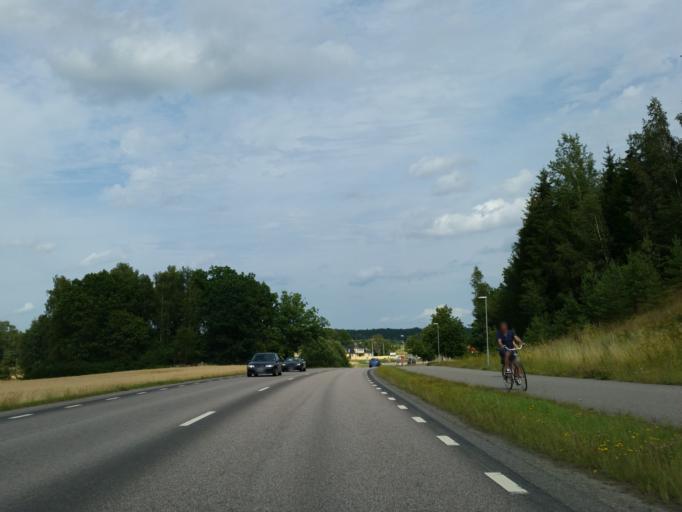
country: SE
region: Soedermanland
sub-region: Strangnas Kommun
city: Mariefred
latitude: 59.2524
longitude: 17.1760
